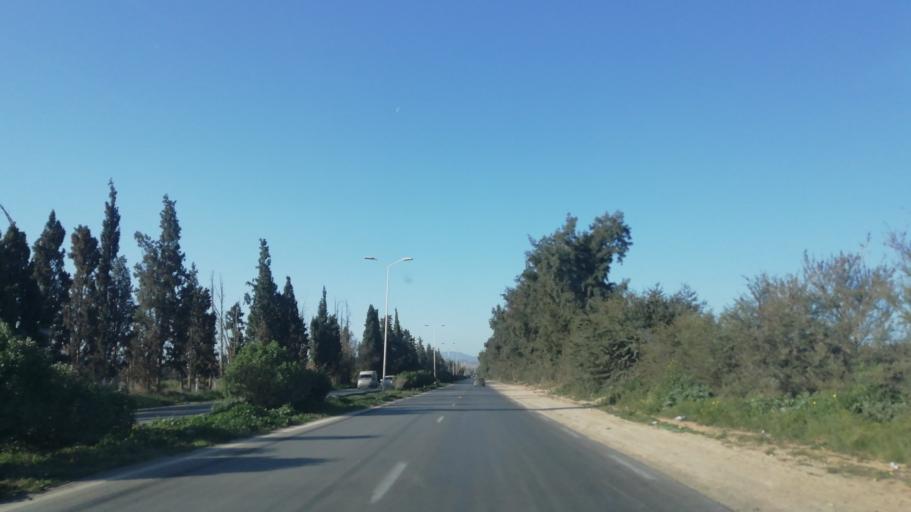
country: DZ
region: Mascara
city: Mascara
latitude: 35.6045
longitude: 0.0890
